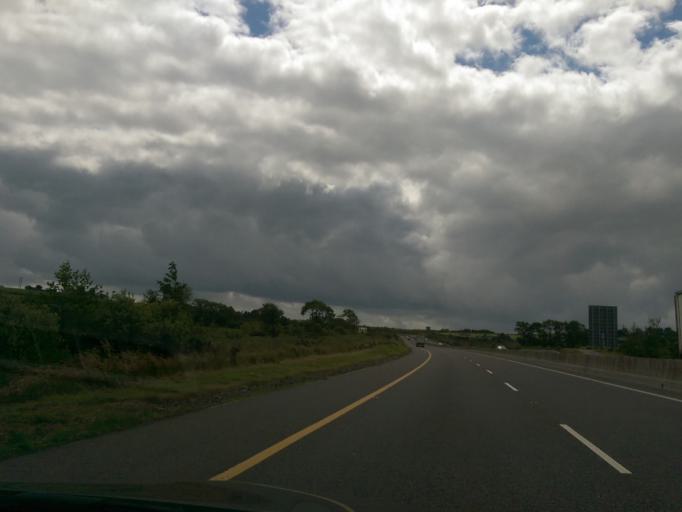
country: IE
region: Munster
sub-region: County Cork
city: Mitchelstown
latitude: 52.2311
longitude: -8.2865
